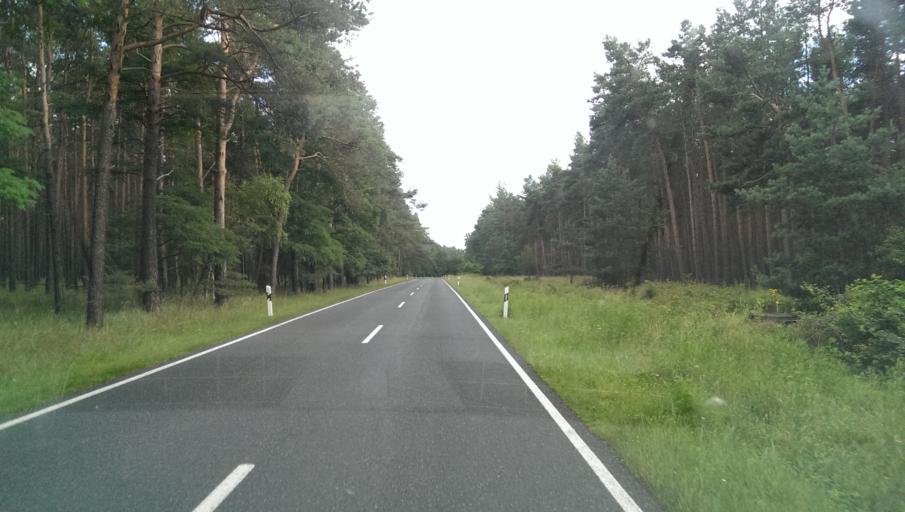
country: DE
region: Saxony-Anhalt
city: Radis
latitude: 51.7735
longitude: 12.4926
